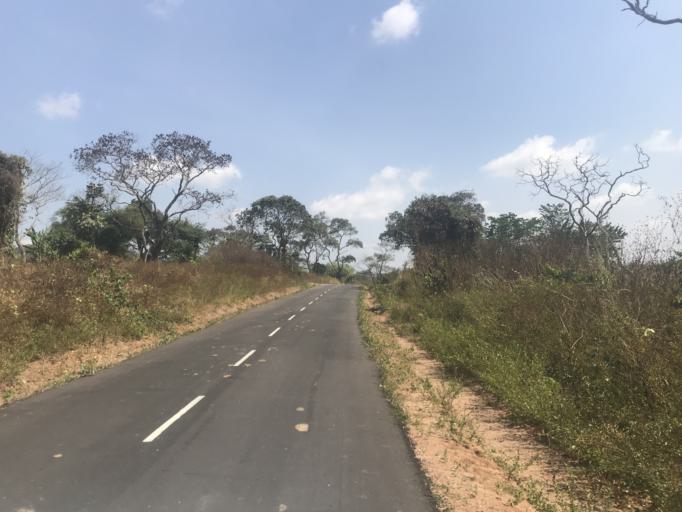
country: NG
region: Osun
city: Otan Ayegbaju
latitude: 7.8964
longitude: 4.8390
